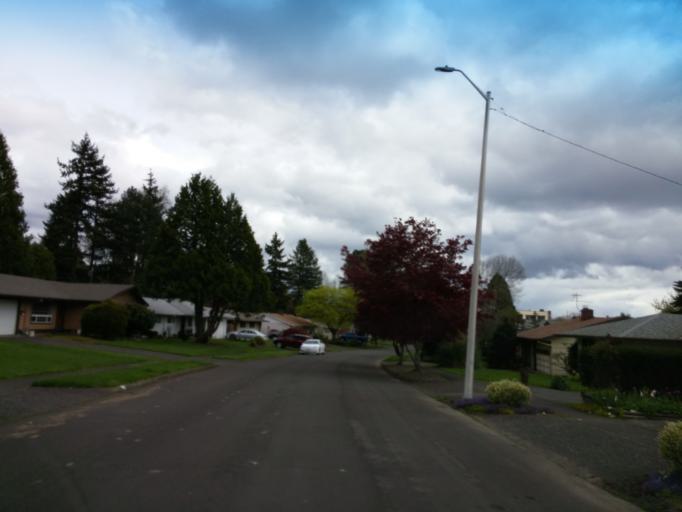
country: US
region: Oregon
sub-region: Washington County
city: Cedar Hills
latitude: 45.5019
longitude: -122.8123
